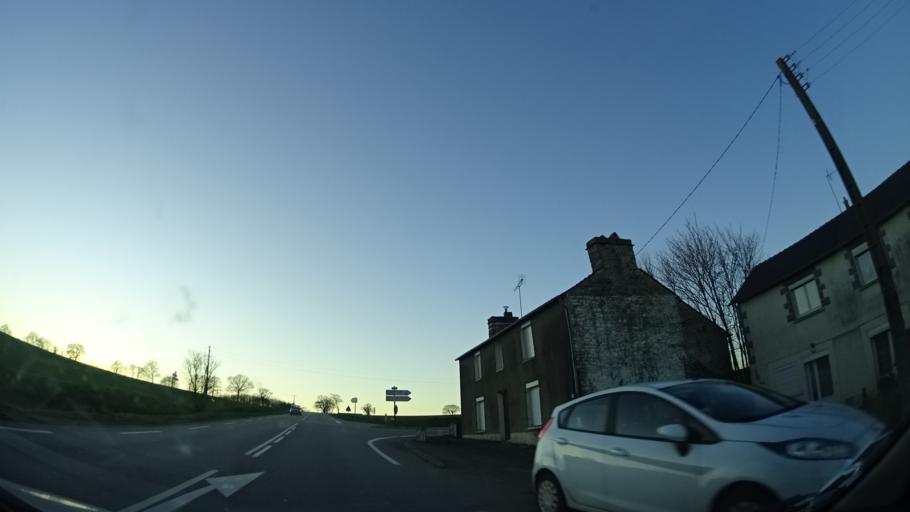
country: FR
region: Brittany
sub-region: Departement d'Ille-et-Vilaine
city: Poce-les-Bois
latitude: 48.1235
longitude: -1.2381
